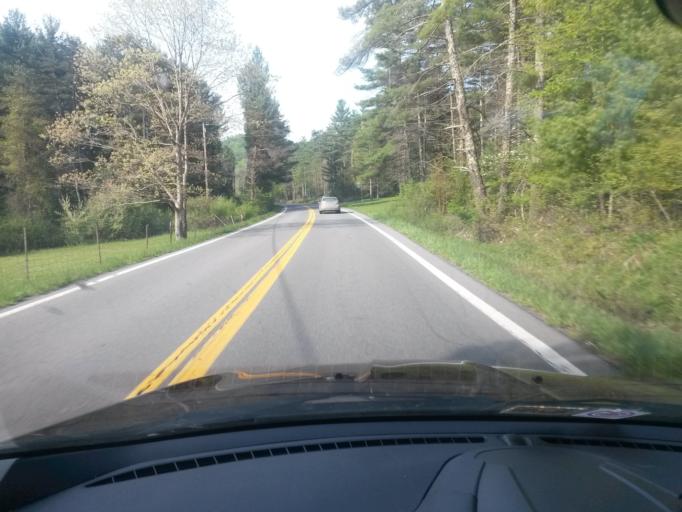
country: US
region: West Virginia
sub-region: Pocahontas County
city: Marlinton
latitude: 38.0466
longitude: -80.0283
